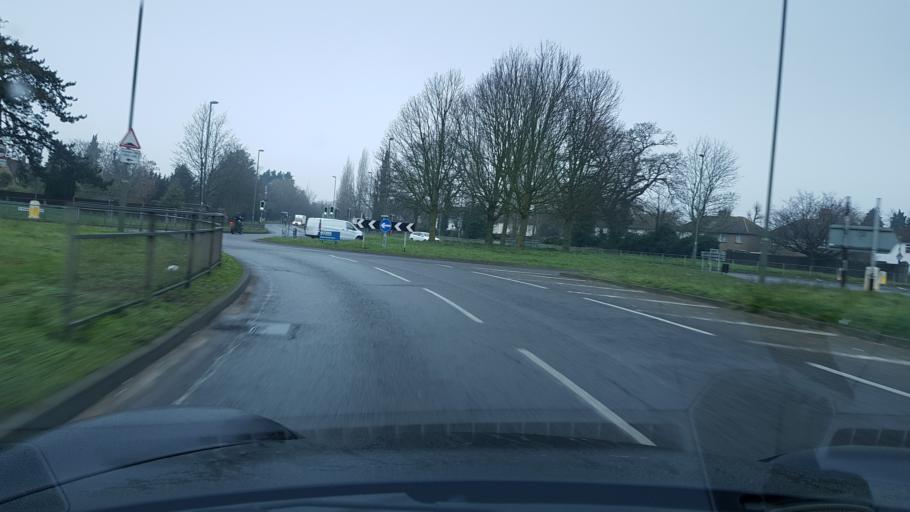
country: GB
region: England
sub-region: Surrey
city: Guildford
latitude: 51.2524
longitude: -0.5718
